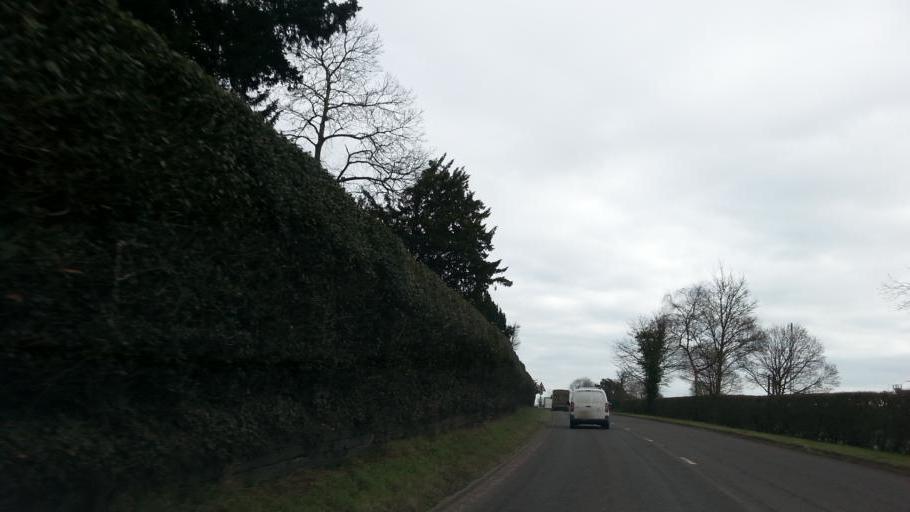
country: GB
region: England
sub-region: Staffordshire
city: Stafford
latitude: 52.8546
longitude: -2.0707
